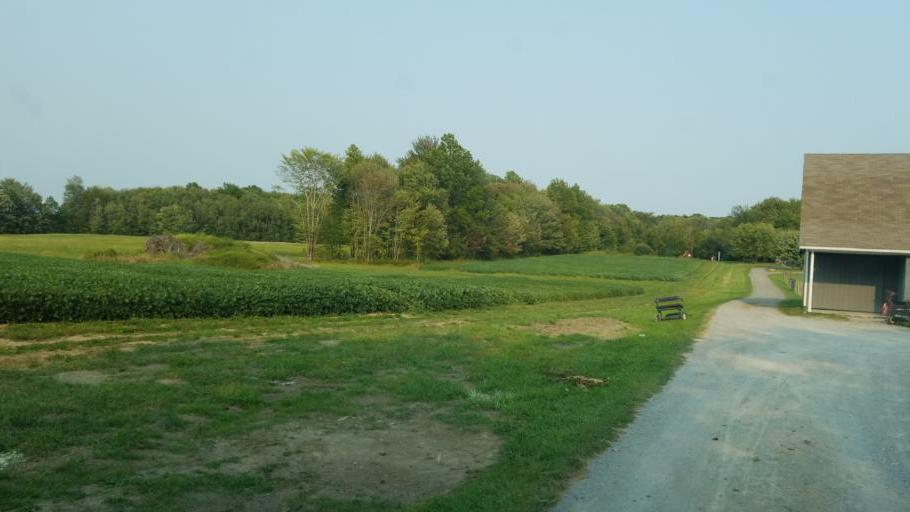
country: US
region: Ohio
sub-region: Geauga County
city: Middlefield
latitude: 41.4015
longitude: -81.0596
